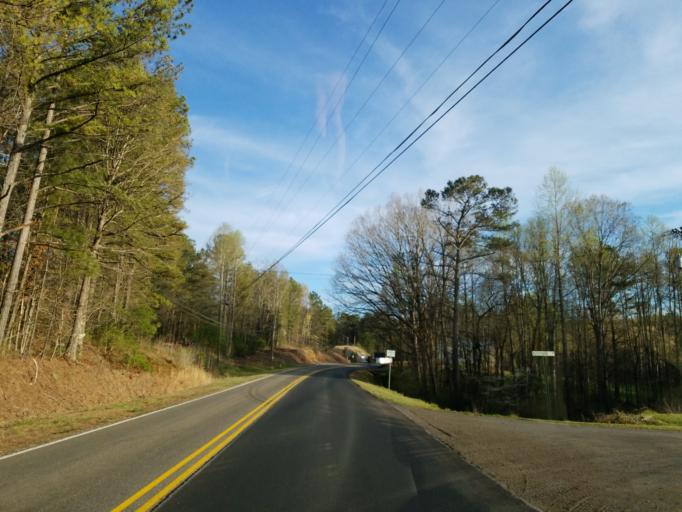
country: US
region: Georgia
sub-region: Pickens County
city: Jasper
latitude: 34.4356
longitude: -84.3964
